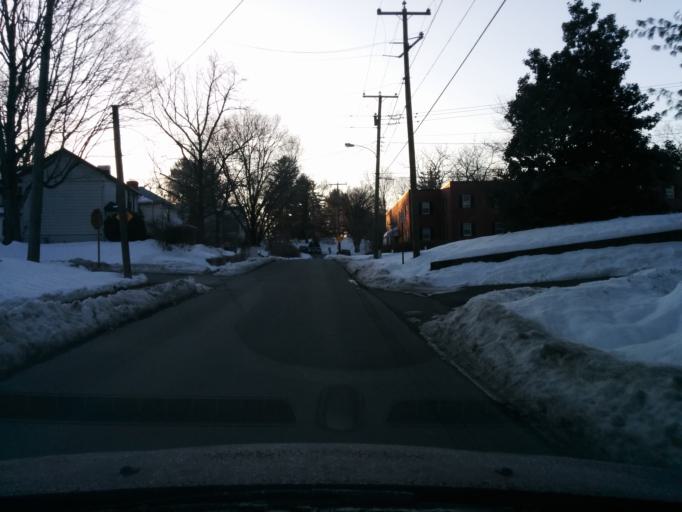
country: US
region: Virginia
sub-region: City of Lexington
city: Lexington
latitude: 37.7832
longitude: -79.4390
